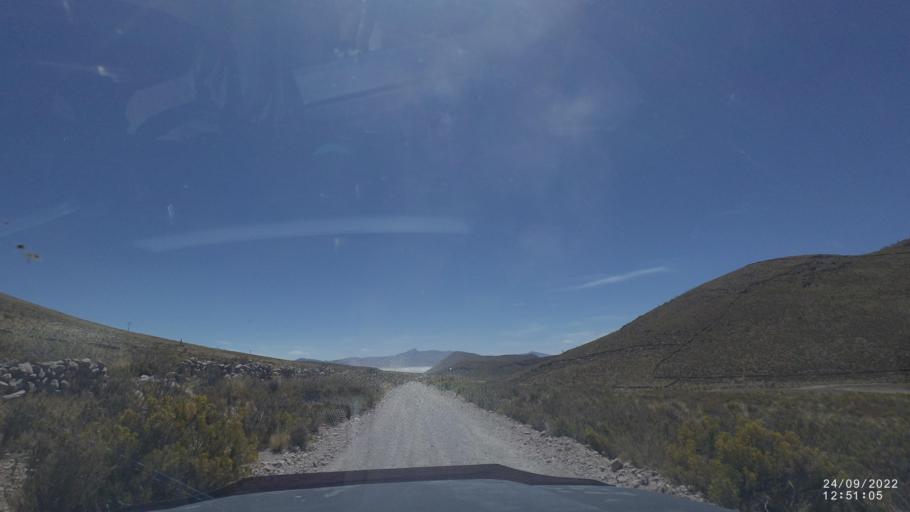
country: BO
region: Potosi
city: Colchani
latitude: -19.8201
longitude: -67.5644
